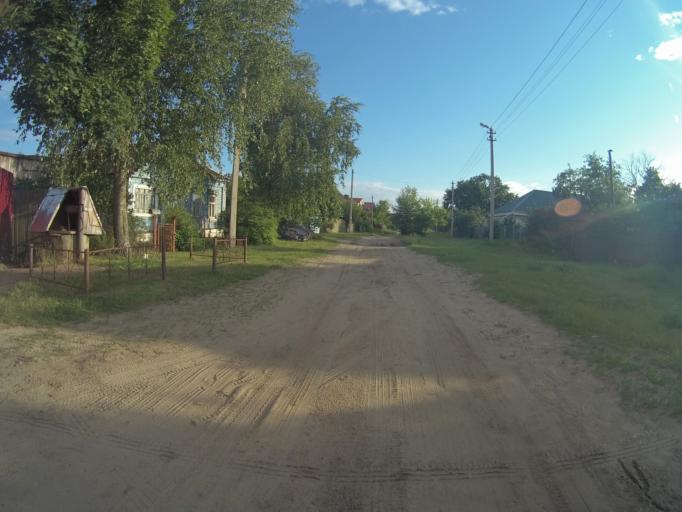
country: RU
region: Vladimir
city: Kommunar
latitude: 56.1179
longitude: 40.4526
